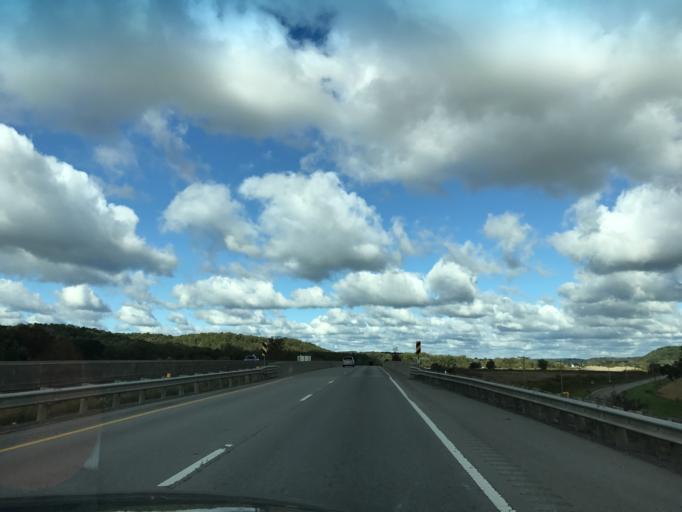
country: US
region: Ohio
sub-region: Hocking County
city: Logan
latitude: 39.5002
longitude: -82.3445
